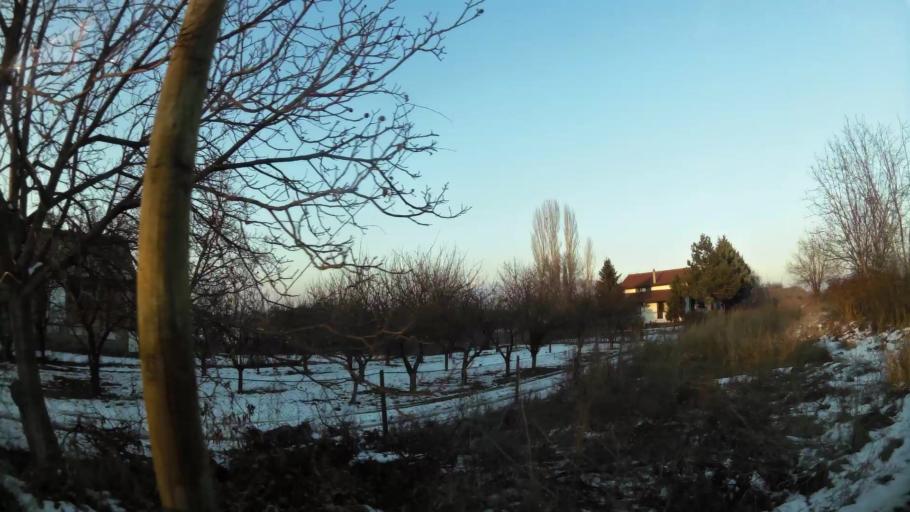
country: MK
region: Kisela Voda
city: Kisela Voda
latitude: 41.9811
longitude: 21.4924
